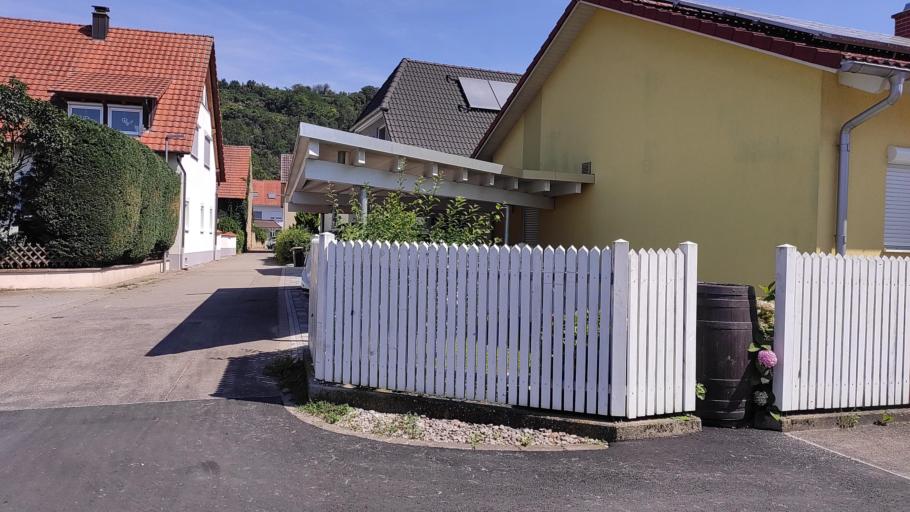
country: DE
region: Baden-Wuerttemberg
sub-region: Freiburg Region
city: Merdingen
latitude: 47.9881
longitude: 7.6697
